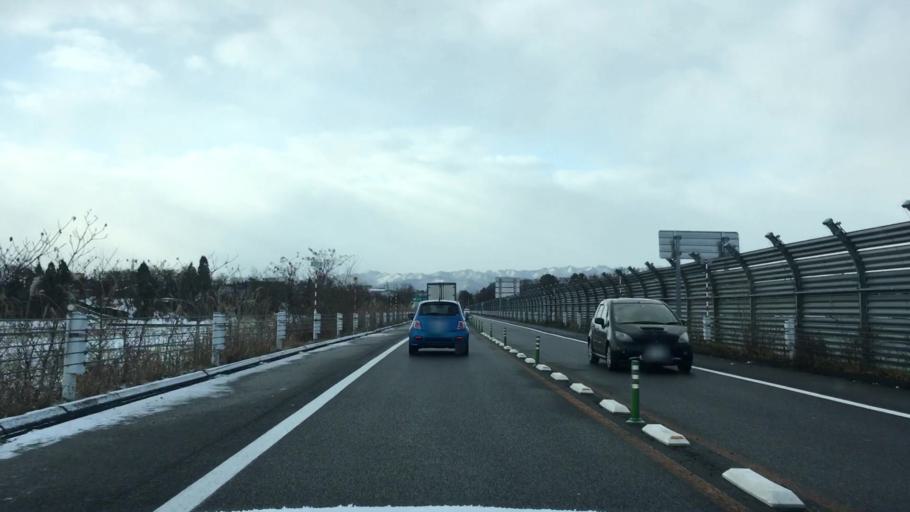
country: JP
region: Akita
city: Odate
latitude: 40.2808
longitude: 140.5388
